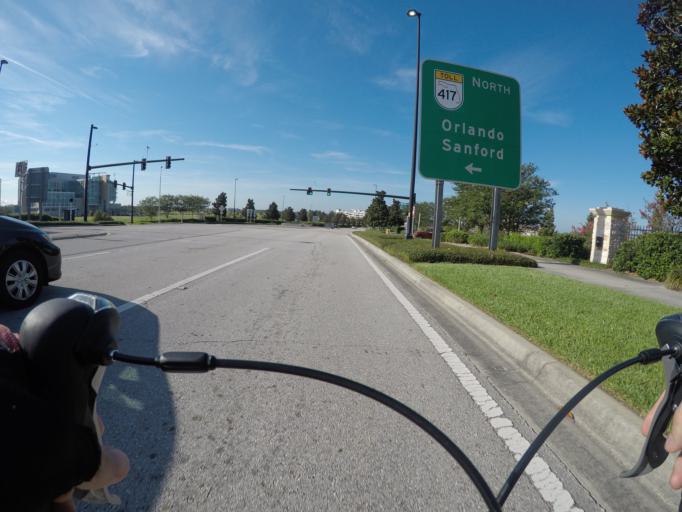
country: US
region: Florida
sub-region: Osceola County
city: Buenaventura Lakes
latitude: 28.3783
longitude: -81.2771
